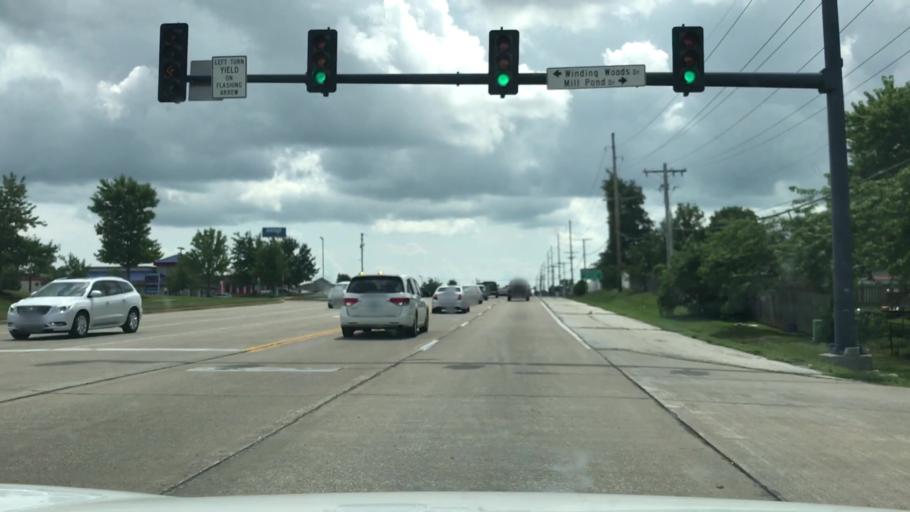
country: US
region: Missouri
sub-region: Saint Charles County
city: O'Fallon
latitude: 38.7837
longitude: -90.6999
